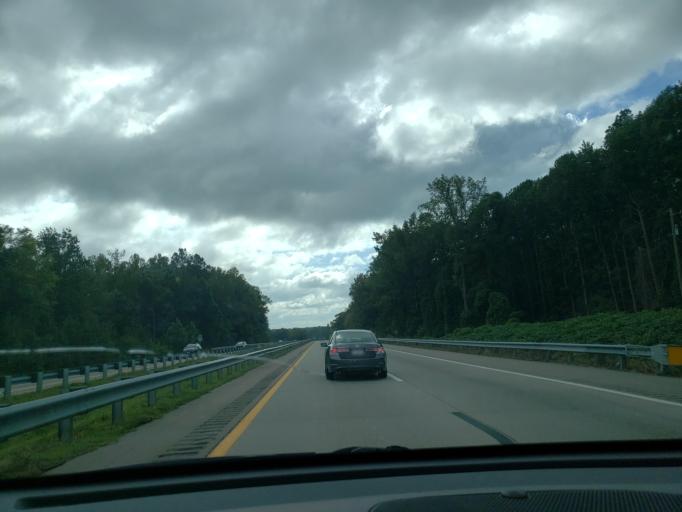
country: US
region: North Carolina
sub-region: Vance County
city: Henderson
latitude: 36.3773
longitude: -78.3543
